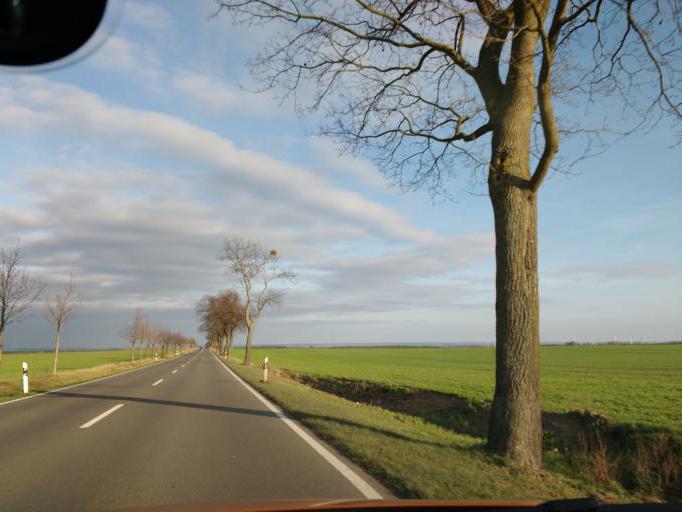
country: DE
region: Brandenburg
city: Wriezen
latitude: 52.6940
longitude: 14.1064
